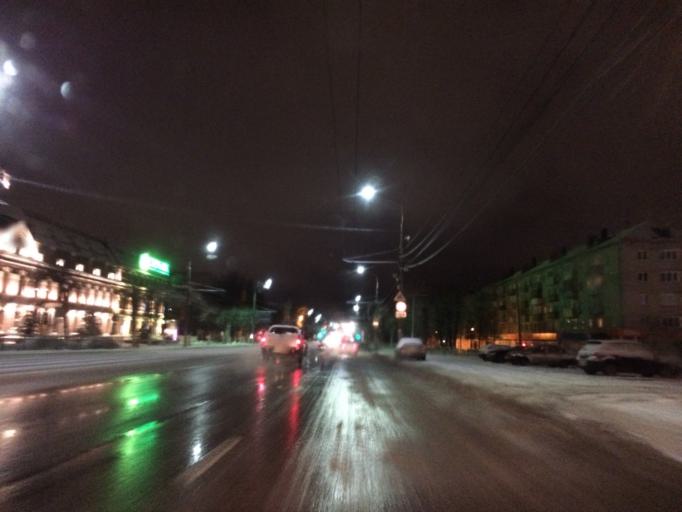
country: RU
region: Tula
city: Tula
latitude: 54.1763
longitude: 37.5990
